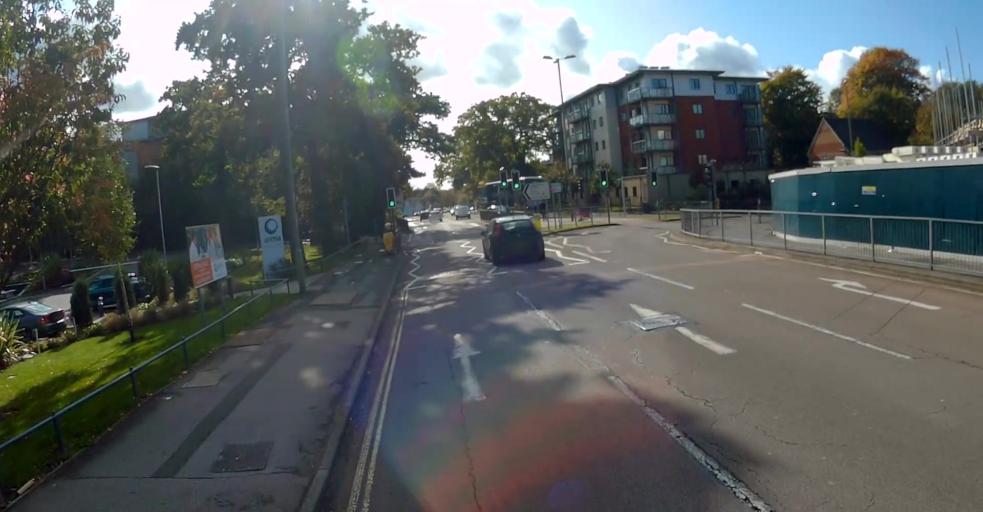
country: GB
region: England
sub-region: Hampshire
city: Farnborough
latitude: 51.2961
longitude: -0.7533
